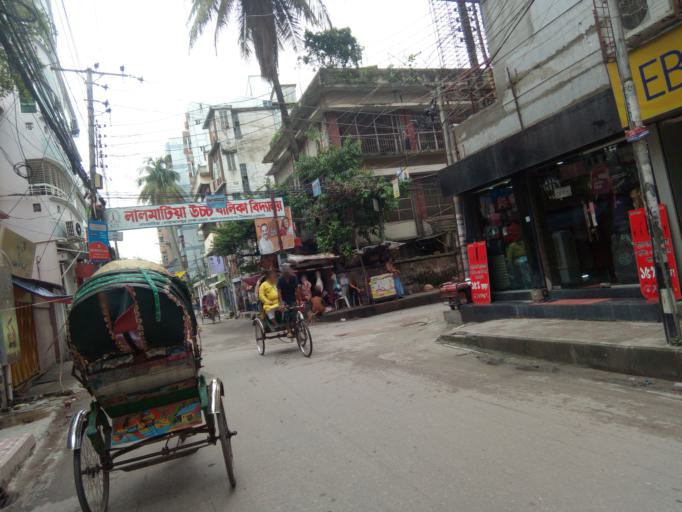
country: BD
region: Dhaka
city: Azimpur
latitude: 23.7573
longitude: 90.3675
